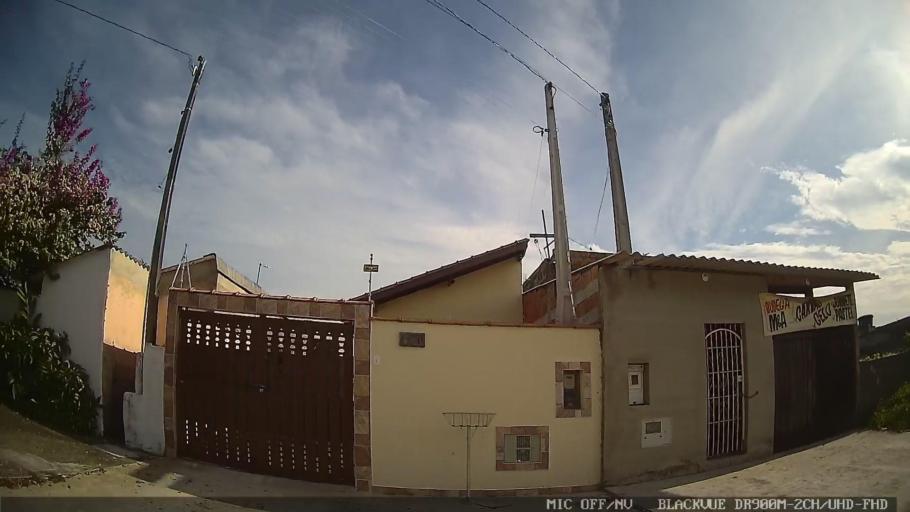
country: BR
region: Sao Paulo
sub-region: Itanhaem
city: Itanhaem
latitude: -24.1660
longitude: -46.7658
